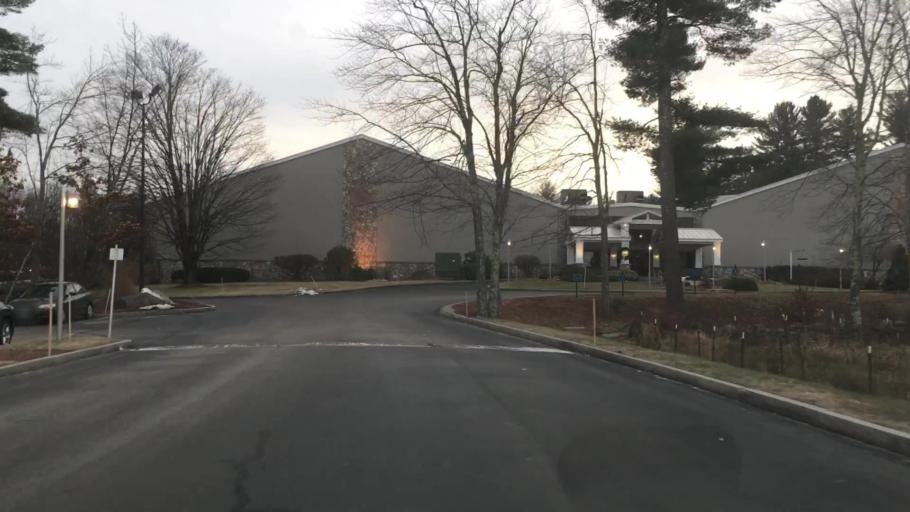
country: US
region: New Hampshire
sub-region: Hillsborough County
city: Milford
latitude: 42.8151
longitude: -71.6369
